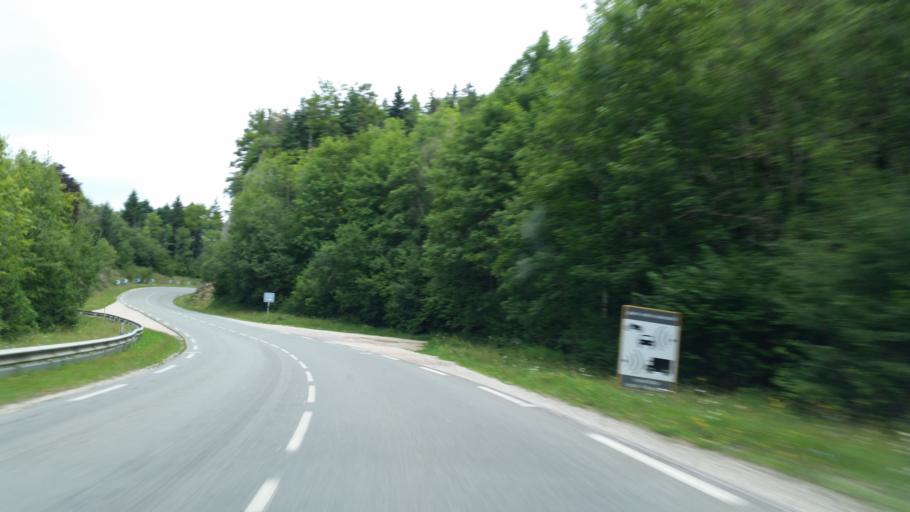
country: FR
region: Franche-Comte
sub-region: Departement du Doubs
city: Maiche
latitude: 47.2612
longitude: 6.8037
